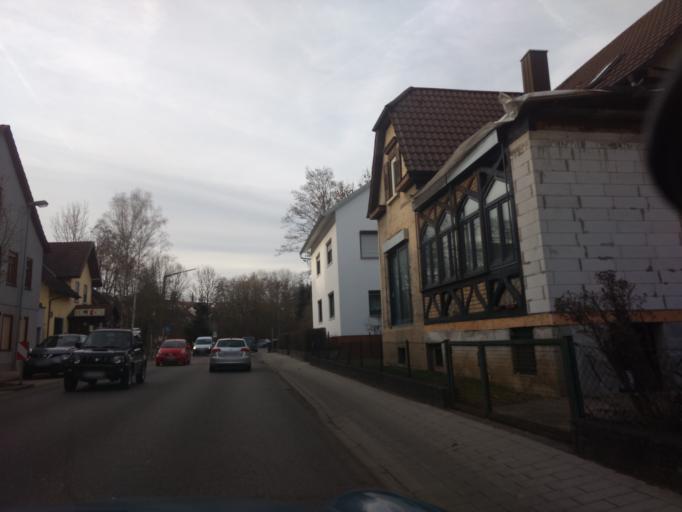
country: DE
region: Baden-Wuerttemberg
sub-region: Regierungsbezirk Stuttgart
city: Rechberghausen
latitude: 48.7330
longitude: 9.6419
